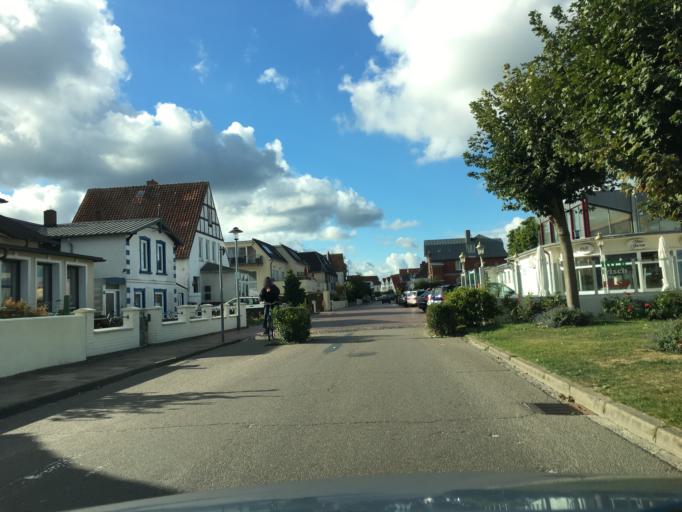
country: DE
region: Schleswig-Holstein
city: Laboe
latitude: 54.4079
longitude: 10.2227
